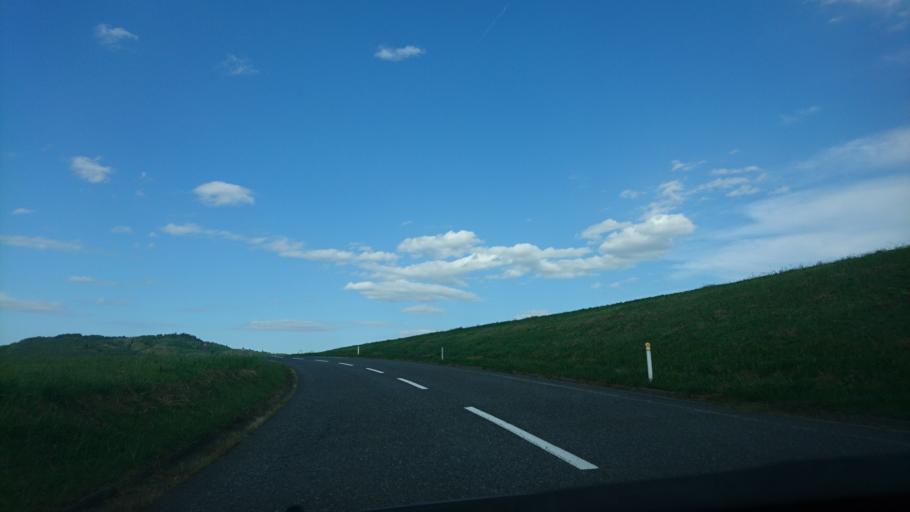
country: JP
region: Iwate
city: Ichinoseki
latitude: 38.8322
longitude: 141.2585
